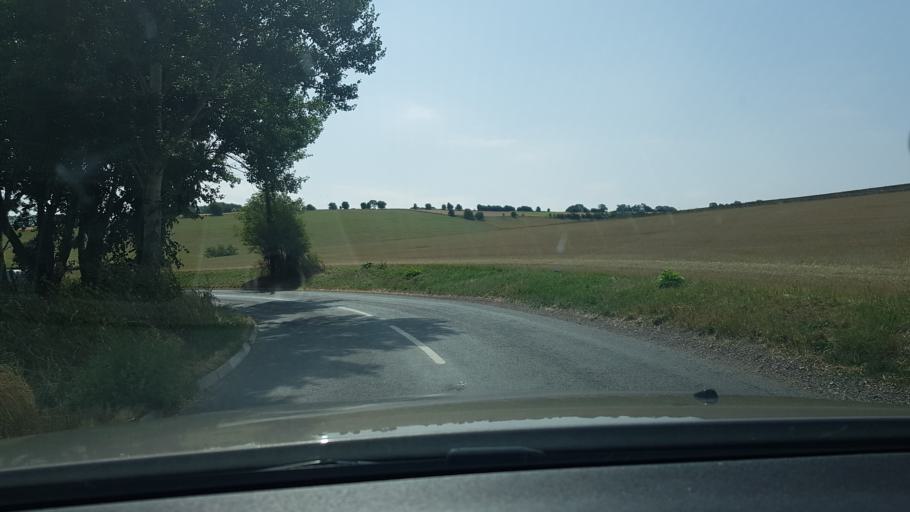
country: GB
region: England
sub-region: West Berkshire
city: Wickham
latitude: 51.4807
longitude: -1.4697
